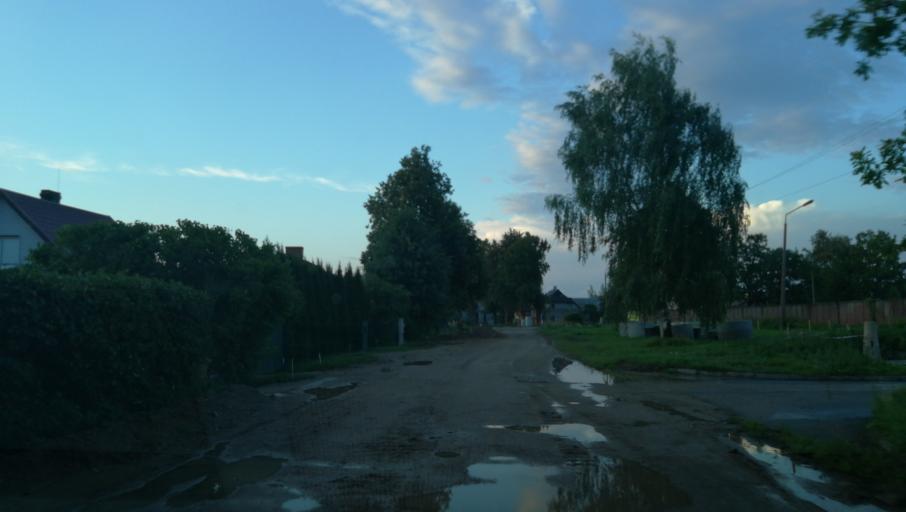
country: LV
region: Cesu Rajons
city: Cesis
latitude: 57.3192
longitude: 25.2967
